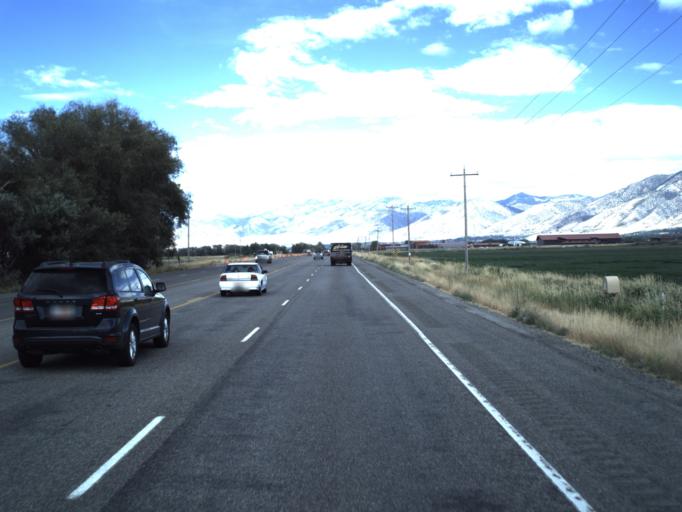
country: US
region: Utah
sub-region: Cache County
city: Wellsville
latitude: 41.6578
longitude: -111.9008
